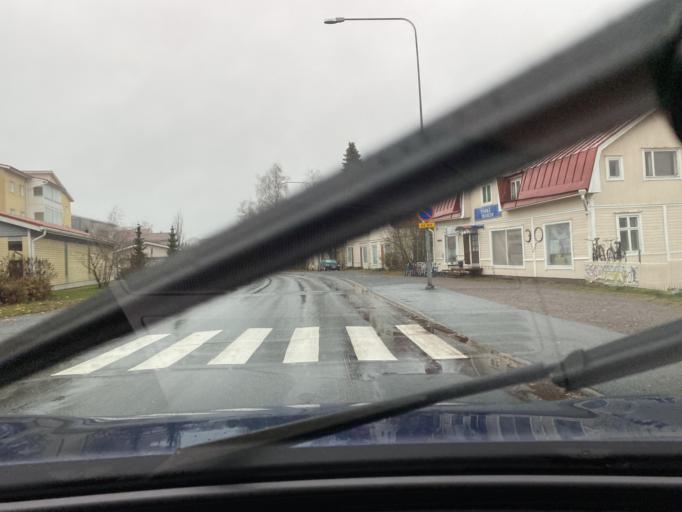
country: FI
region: Varsinais-Suomi
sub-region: Loimaa
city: Loimaa
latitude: 60.8534
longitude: 23.0562
